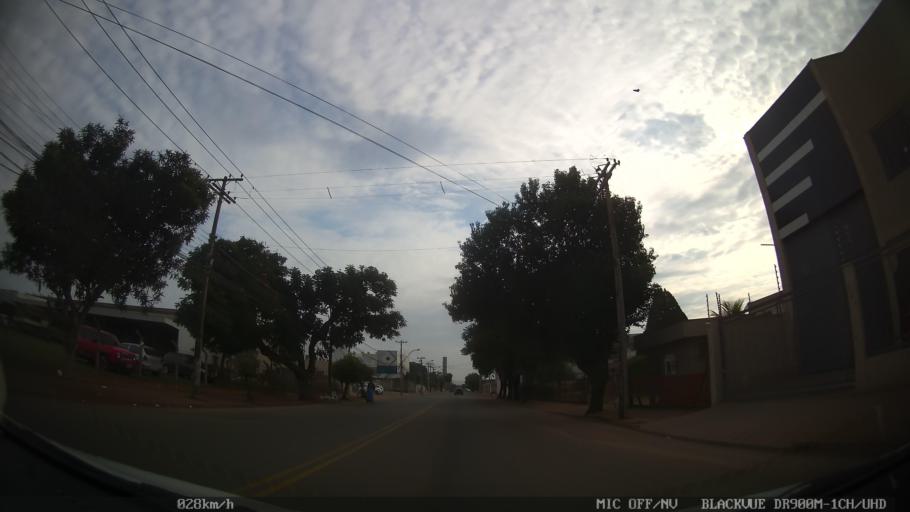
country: BR
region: Sao Paulo
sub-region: Santa Barbara D'Oeste
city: Santa Barbara d'Oeste
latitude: -22.7601
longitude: -47.3862
